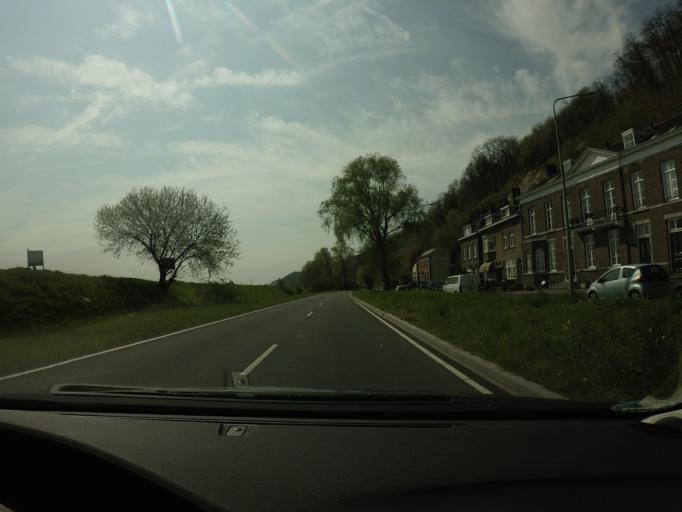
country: NL
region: Limburg
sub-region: Gemeente Maastricht
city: Maastricht
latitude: 50.8152
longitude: 5.6939
